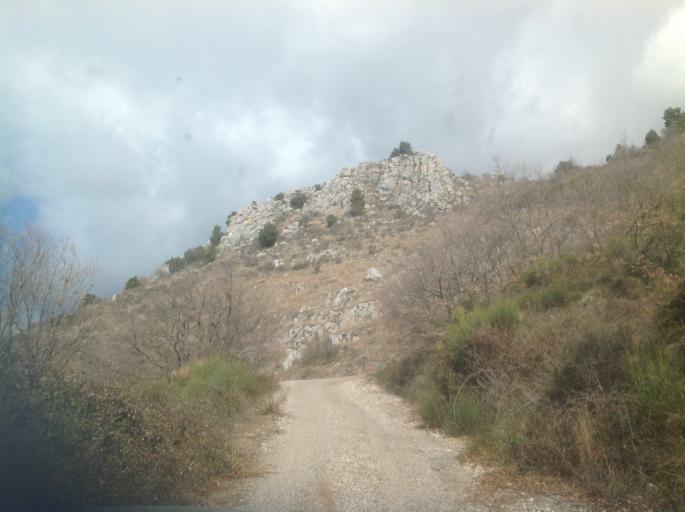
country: IT
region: Calabria
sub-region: Provincia di Cosenza
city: Frascineto
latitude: 39.8458
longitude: 16.2601
